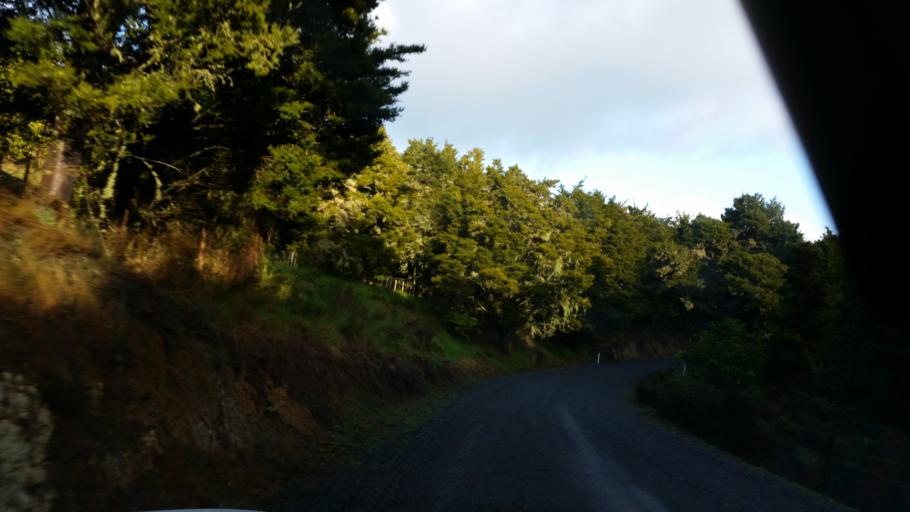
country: NZ
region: Northland
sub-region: Whangarei
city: Maungatapere
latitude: -35.7793
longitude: 174.0927
